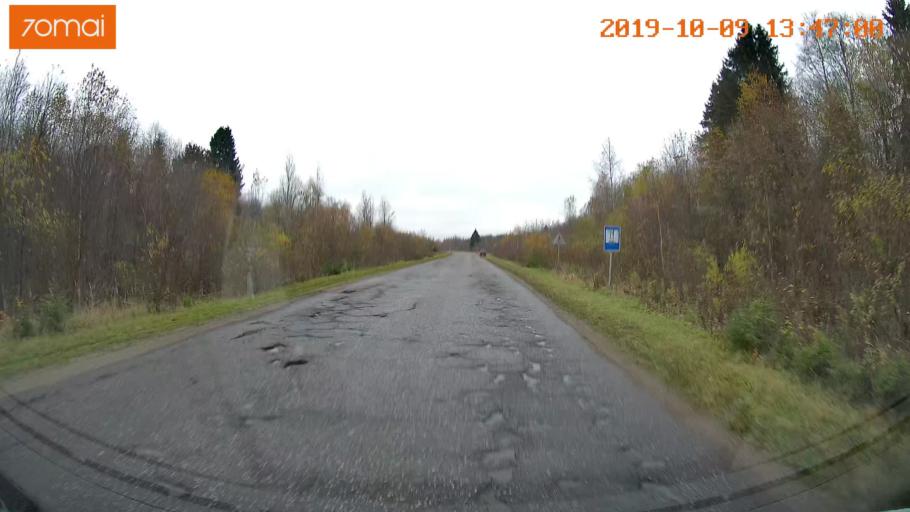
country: RU
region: Kostroma
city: Buy
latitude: 58.3882
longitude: 41.2218
